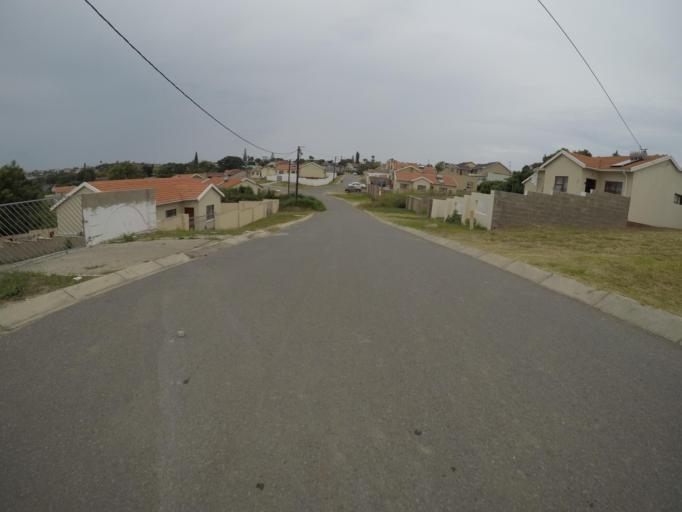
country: ZA
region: Eastern Cape
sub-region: Buffalo City Metropolitan Municipality
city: East London
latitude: -33.0025
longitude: 27.8547
